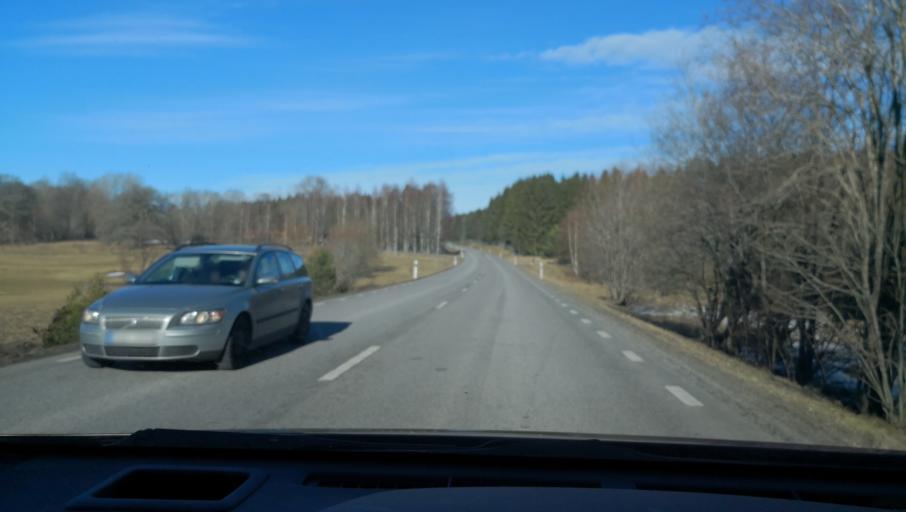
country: SE
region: Uppsala
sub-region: Uppsala Kommun
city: Vattholma
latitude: 60.0278
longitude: 17.7496
